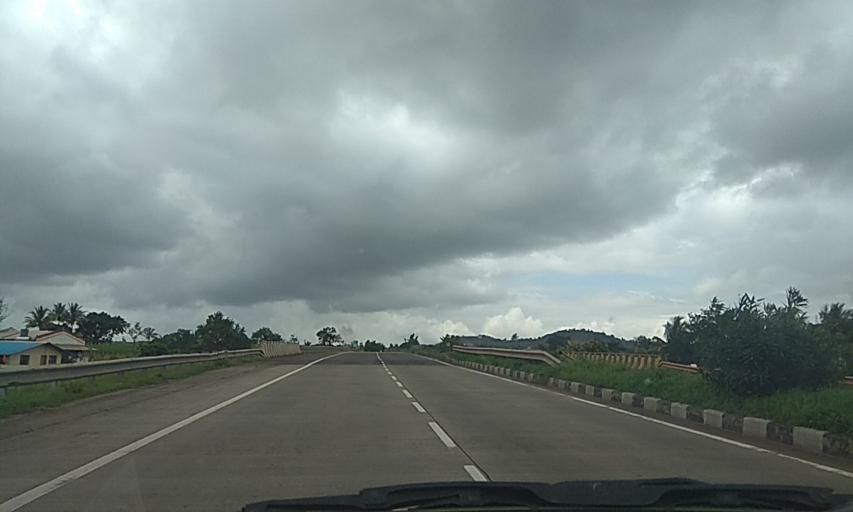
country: IN
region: Karnataka
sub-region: Belgaum
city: Sankeshwar
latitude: 16.2551
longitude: 74.4707
